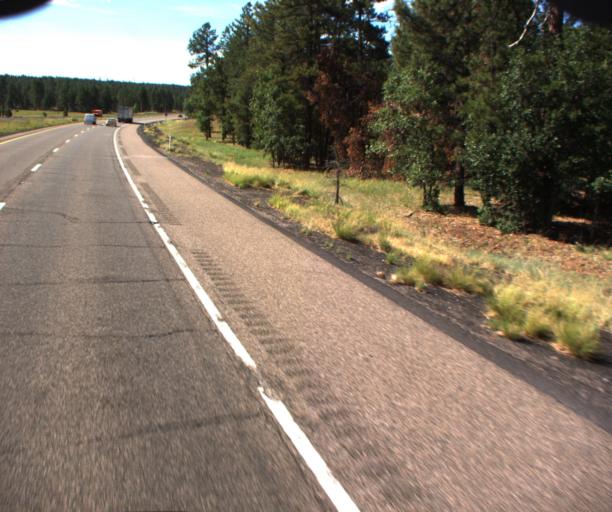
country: US
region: Arizona
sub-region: Coconino County
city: Sedona
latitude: 34.8478
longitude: -111.6046
